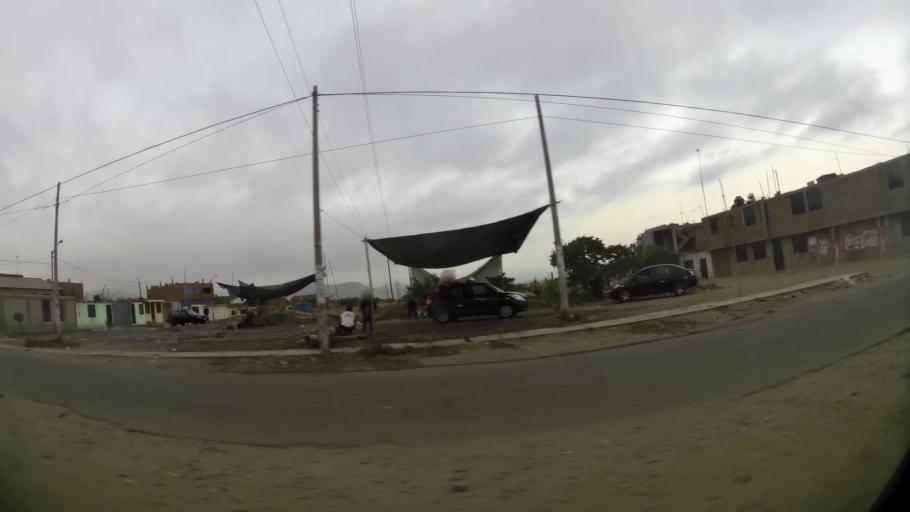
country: PE
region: La Libertad
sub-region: Provincia de Trujillo
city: El Porvenir
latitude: -8.0748
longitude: -79.0205
